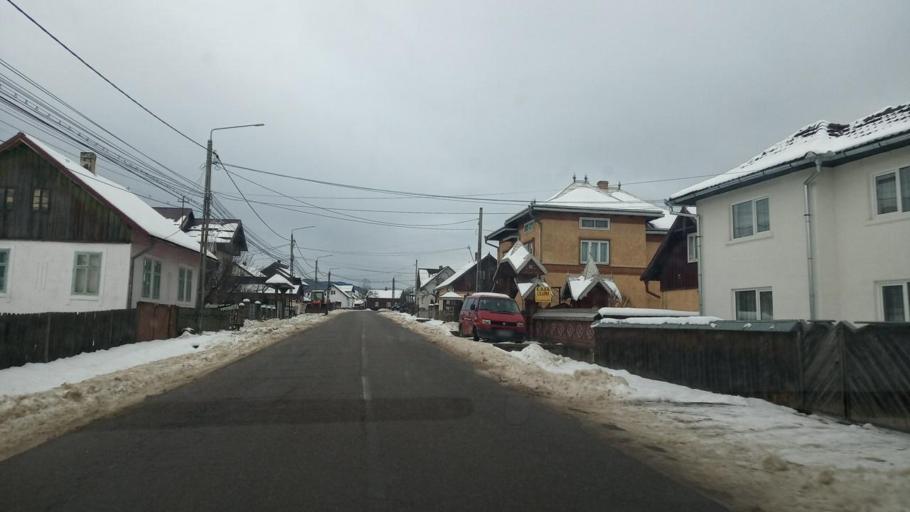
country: RO
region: Suceava
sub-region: Comuna Manastirea Humorului
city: Manastirea Humorului
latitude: 47.5799
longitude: 25.8729
